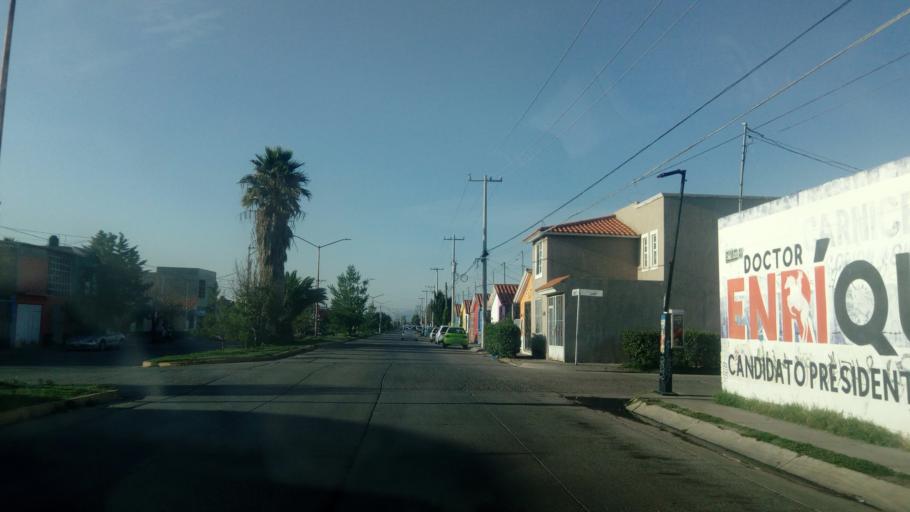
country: MX
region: Durango
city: Victoria de Durango
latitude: 24.0717
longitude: -104.5872
